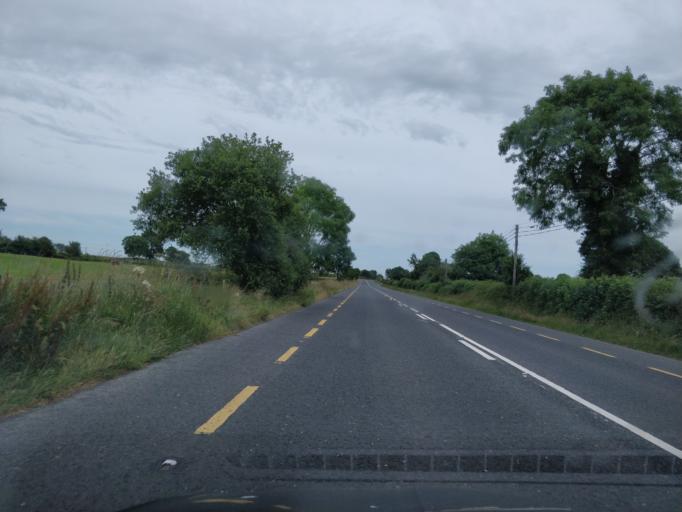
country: IE
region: Leinster
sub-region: Uibh Fhaili
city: Birr
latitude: 53.1553
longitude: -7.8304
